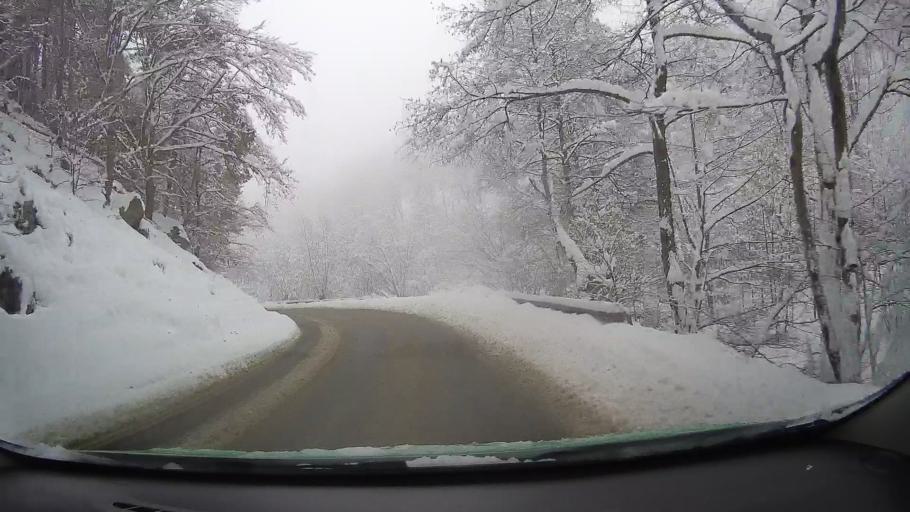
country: RO
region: Sibiu
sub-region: Comuna Tilisca
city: Tilisca
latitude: 45.8022
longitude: 23.8195
